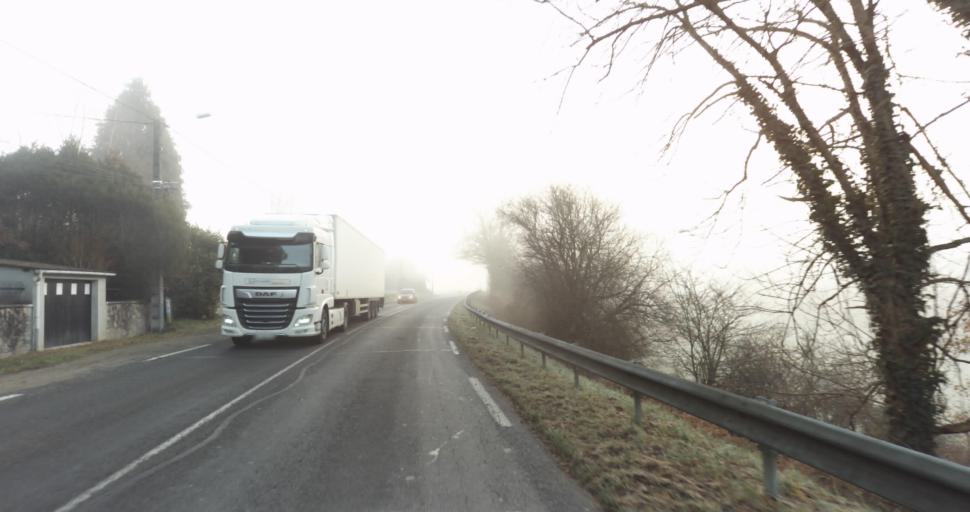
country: FR
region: Limousin
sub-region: Departement de la Haute-Vienne
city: Aixe-sur-Vienne
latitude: 45.7913
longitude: 1.1587
